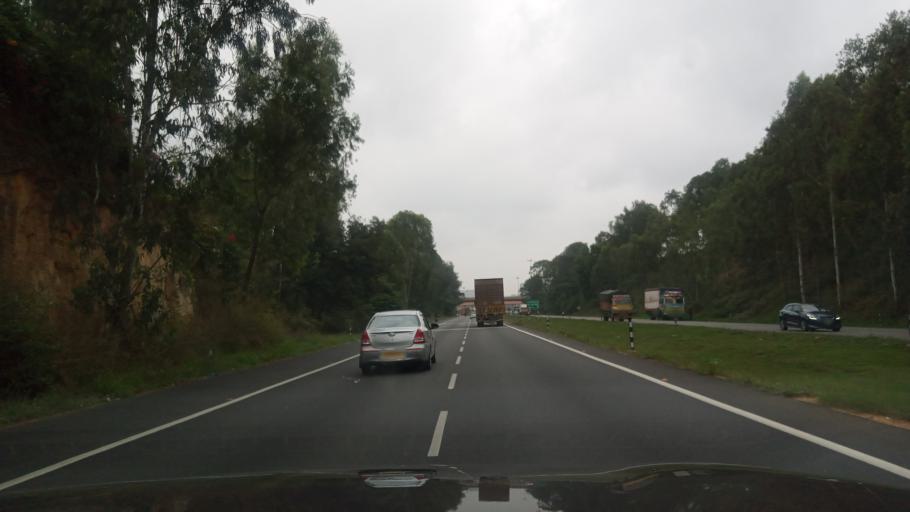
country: IN
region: Karnataka
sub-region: Bangalore Urban
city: Bangalore
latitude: 12.8611
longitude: 77.6512
